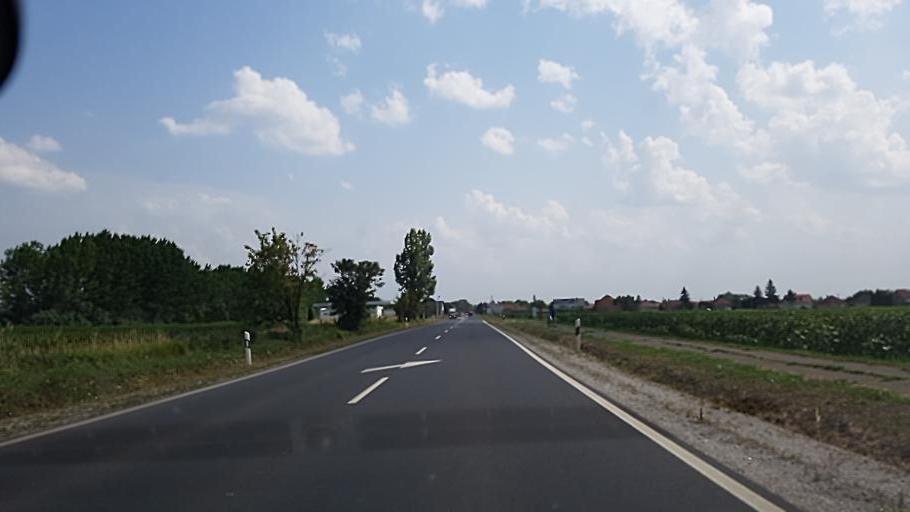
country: HU
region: Heves
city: Besenyotelek
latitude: 47.7123
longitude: 20.4236
